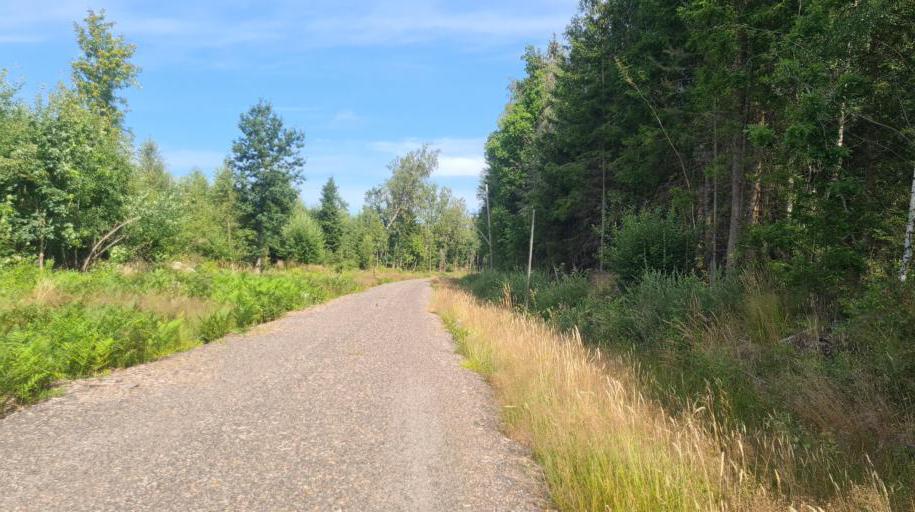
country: SE
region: Kronoberg
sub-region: Ljungby Kommun
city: Lagan
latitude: 56.9843
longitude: 13.9444
